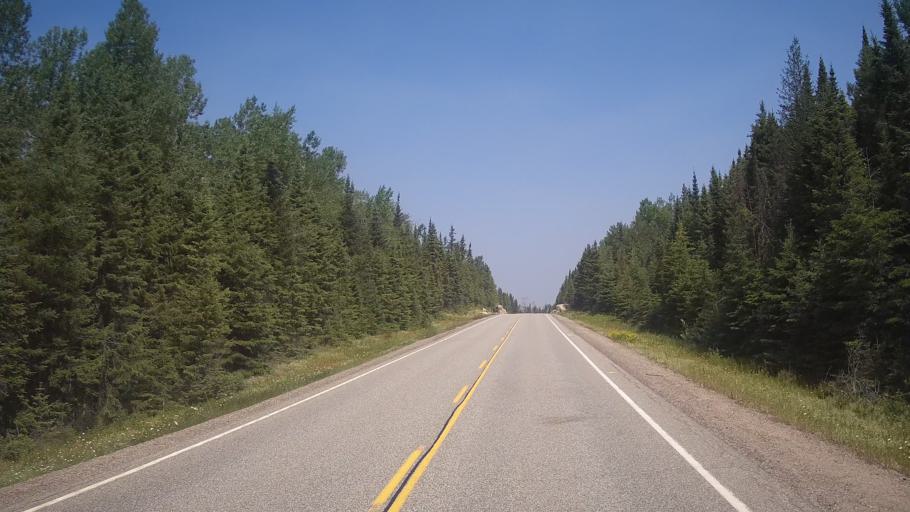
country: CA
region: Ontario
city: Timmins
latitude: 48.0421
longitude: -81.5834
